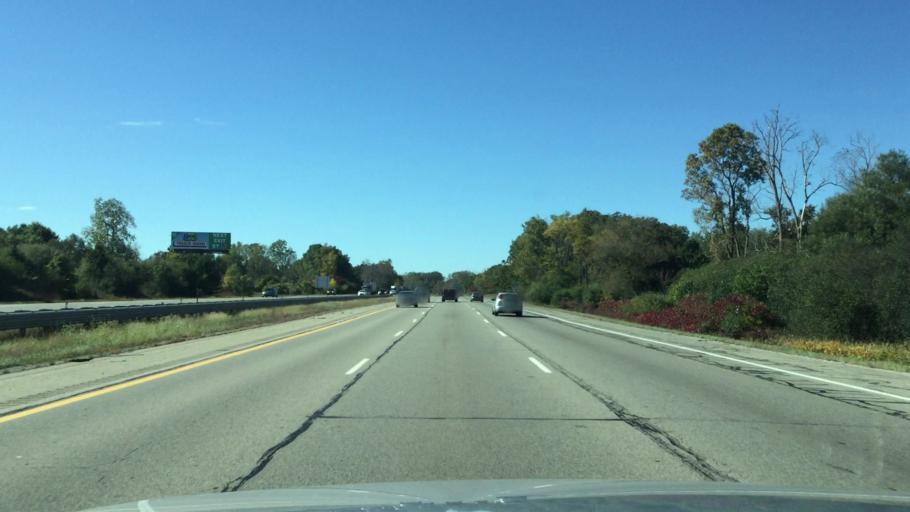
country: US
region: Michigan
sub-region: Washtenaw County
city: Dexter
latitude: 42.2938
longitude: -83.8451
